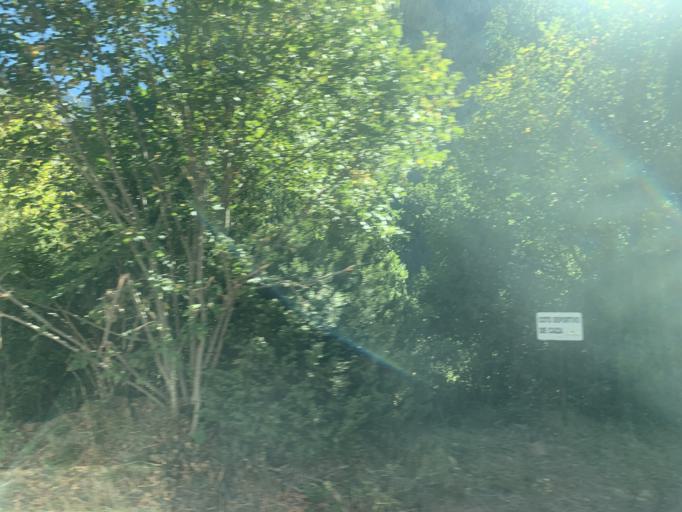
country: ES
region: Aragon
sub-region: Provincia de Huesca
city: Broto
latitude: 42.6426
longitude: -0.1066
